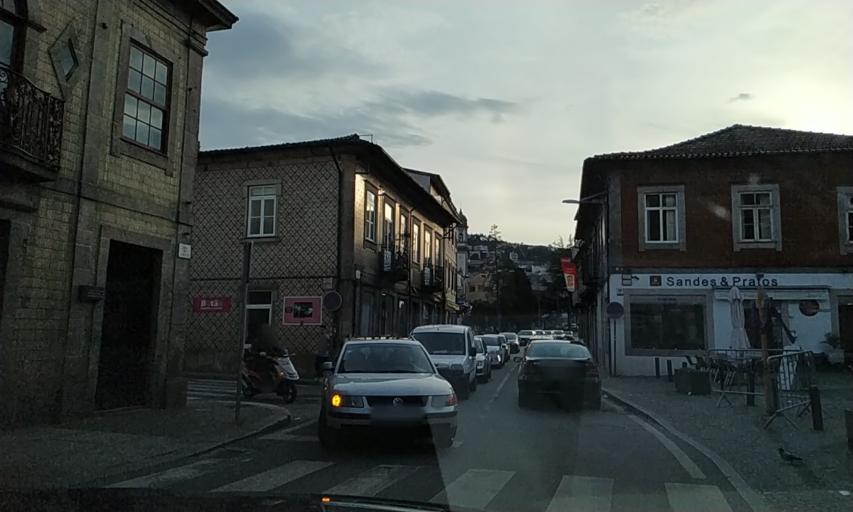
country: PT
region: Porto
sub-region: Valongo
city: Valongo
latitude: 41.1893
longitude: -8.4985
